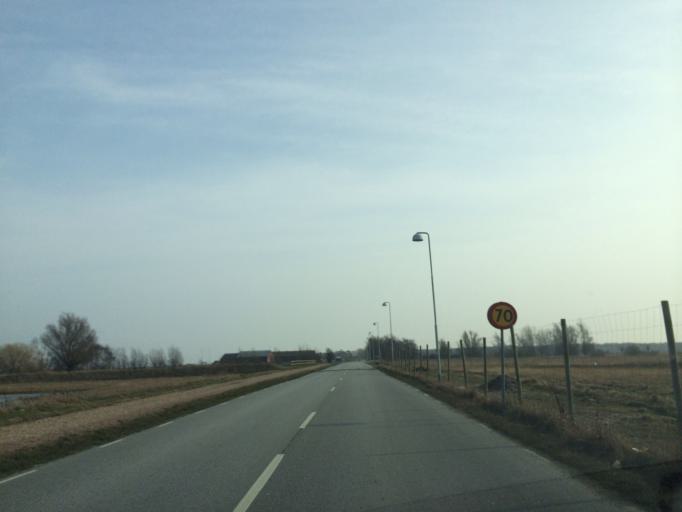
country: SE
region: Skane
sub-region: Vellinge Kommun
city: Skanor med Falsterbo
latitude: 55.4159
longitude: 12.8639
